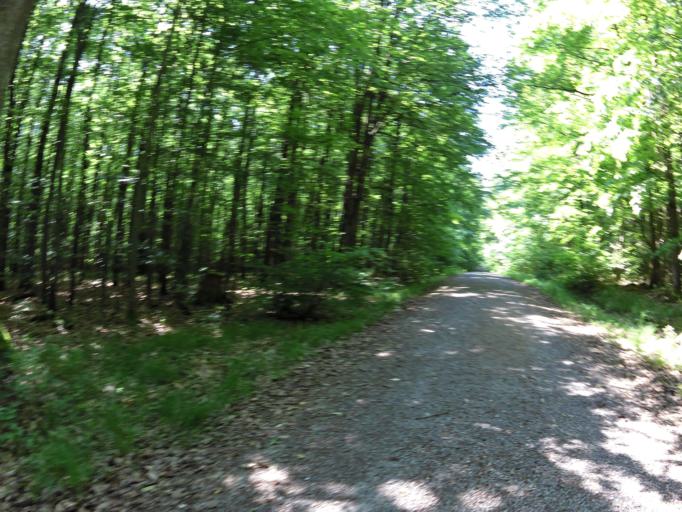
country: DE
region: Bavaria
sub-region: Regierungsbezirk Unterfranken
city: Kist
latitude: 49.7287
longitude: 9.8672
